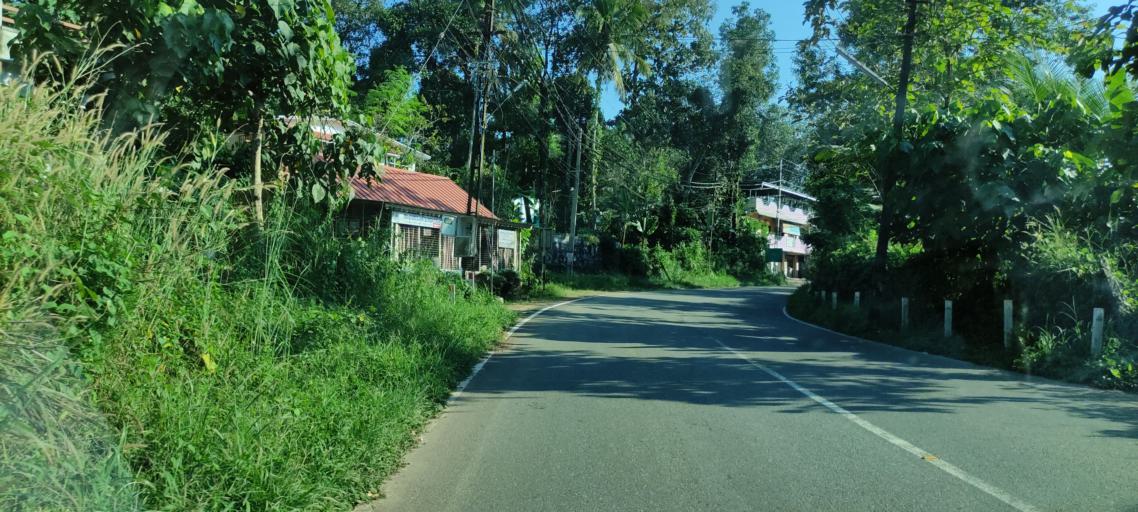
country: IN
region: Kerala
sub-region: Pattanamtitta
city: Adur
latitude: 9.1725
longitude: 76.7416
